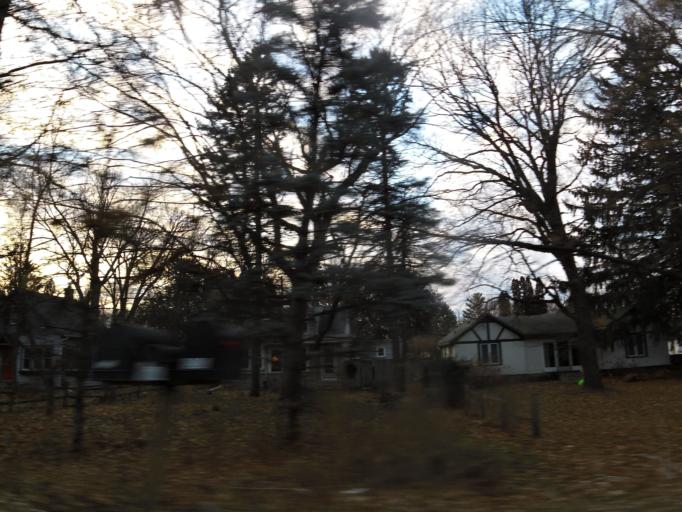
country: US
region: Minnesota
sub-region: Washington County
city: Mahtomedi
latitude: 45.0669
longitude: -92.9574
